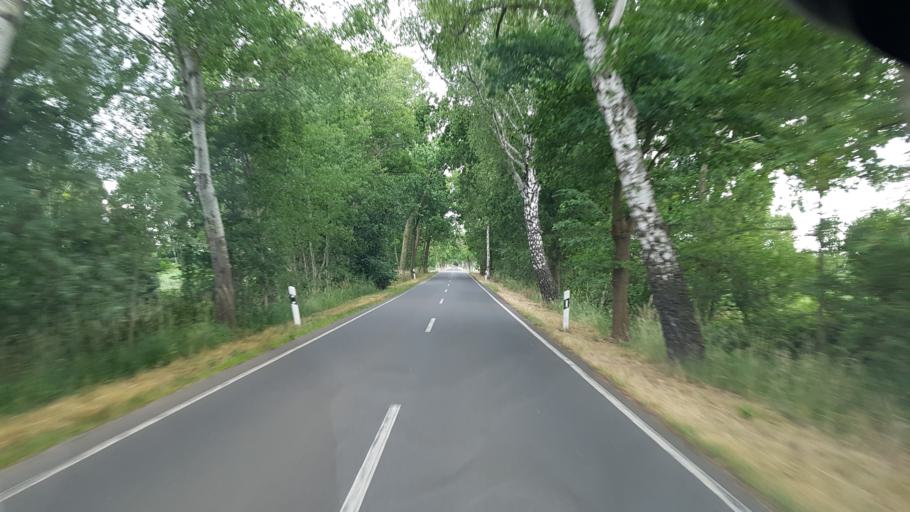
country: DE
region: Brandenburg
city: Kasel-Golzig
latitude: 51.9665
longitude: 13.6753
